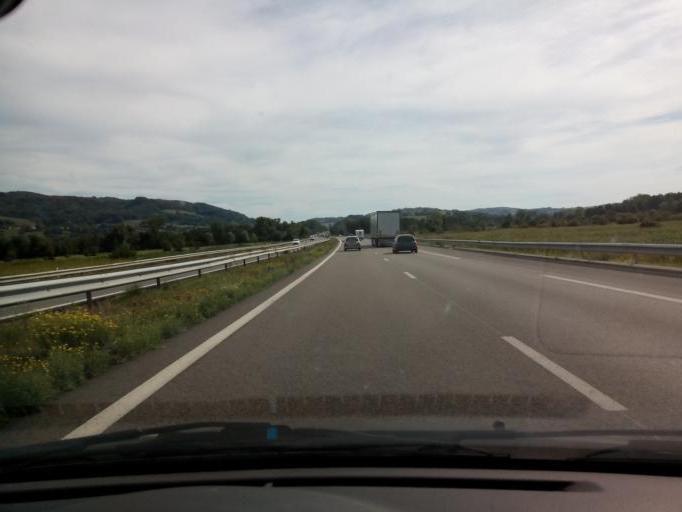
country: FR
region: Rhone-Alpes
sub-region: Departement de l'Isere
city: Saint-Victor-de-Cessieu
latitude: 45.4997
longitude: 5.3992
